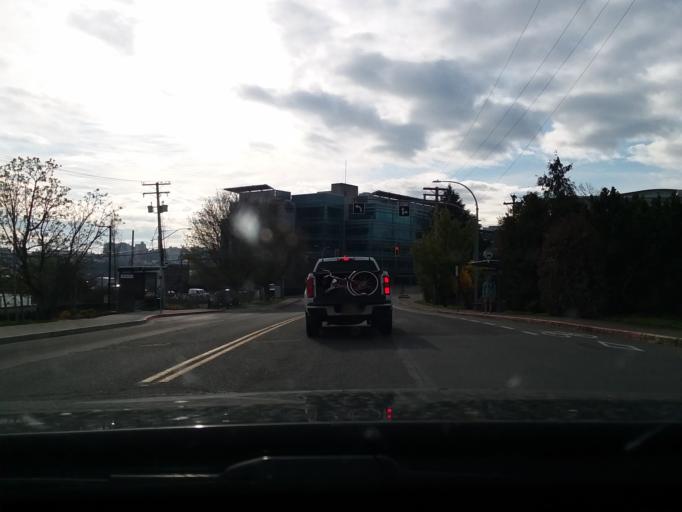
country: CA
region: British Columbia
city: Victoria
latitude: 48.4343
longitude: -123.3816
